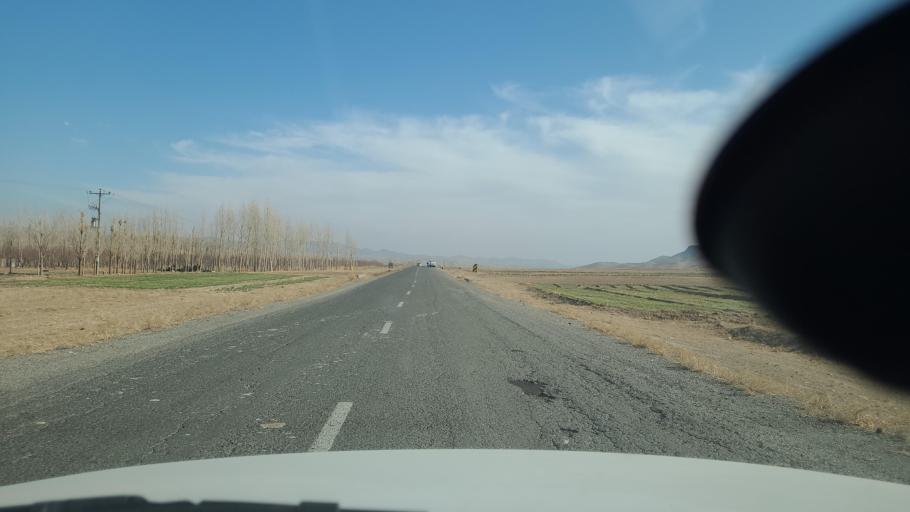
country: IR
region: Razavi Khorasan
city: Fariman
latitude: 35.5882
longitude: 59.6587
